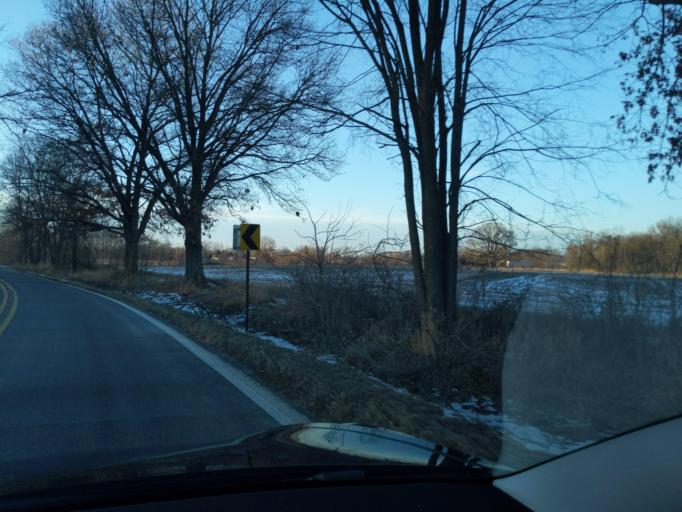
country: US
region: Michigan
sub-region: Ingham County
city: Stockbridge
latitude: 42.4953
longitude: -84.2252
